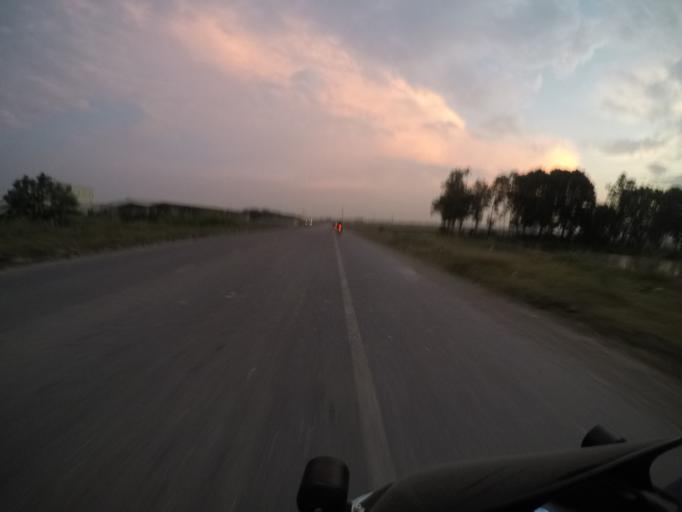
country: VN
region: Vinh Phuc
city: Phuc Yen
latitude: 21.2500
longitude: 105.7215
